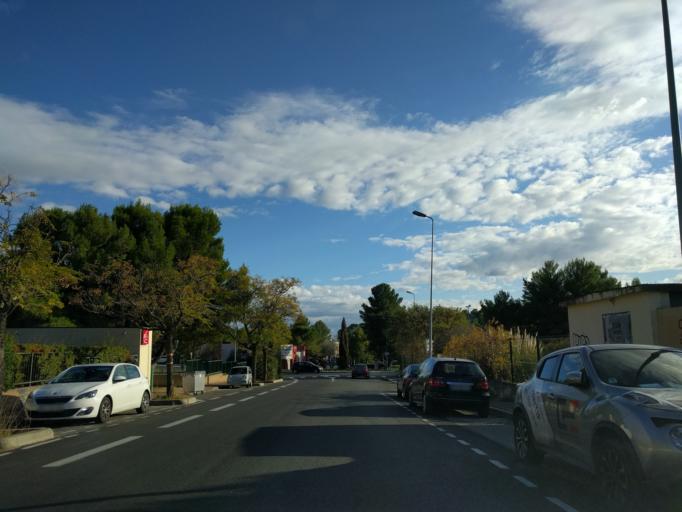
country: FR
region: Languedoc-Roussillon
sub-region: Departement de l'Herault
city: Montferrier-sur-Lez
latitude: 43.6452
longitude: 3.8413
